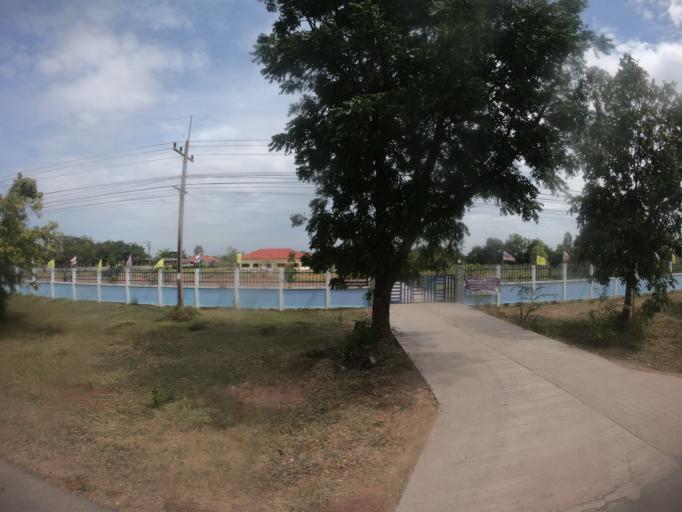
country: TH
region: Maha Sarakham
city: Chiang Yuen
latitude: 16.3623
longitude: 103.1094
